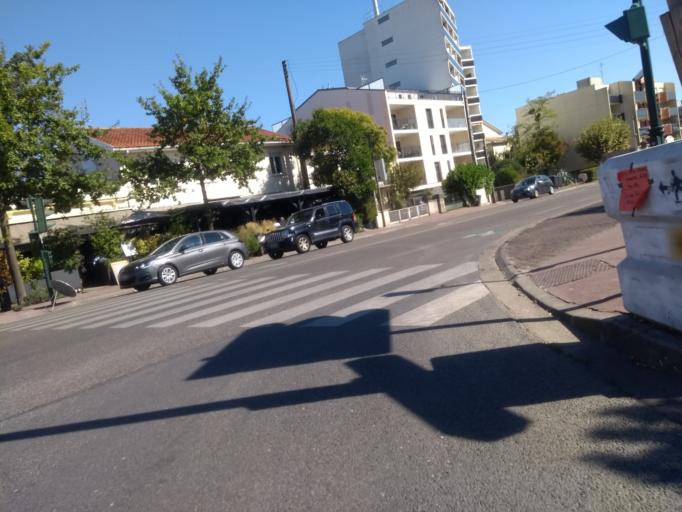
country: FR
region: Aquitaine
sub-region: Departement de la Gironde
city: Bruges
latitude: 44.8582
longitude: -0.6233
